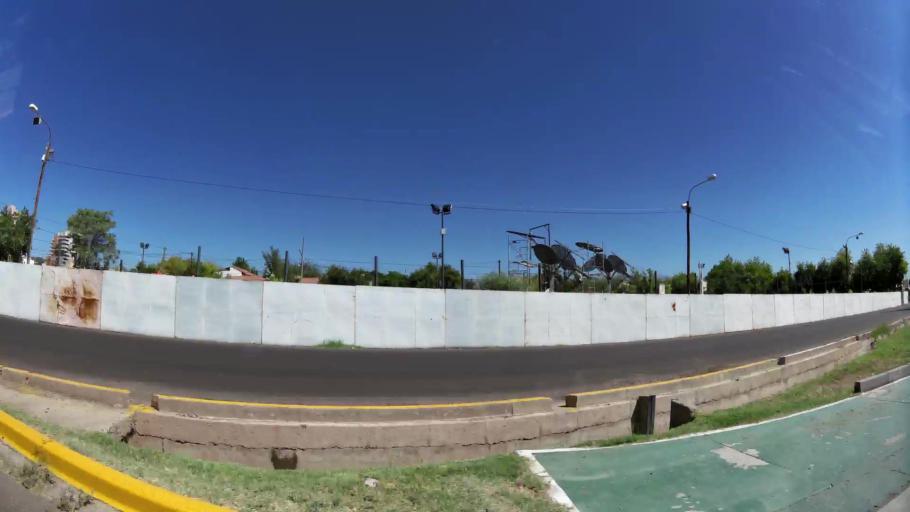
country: AR
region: Mendoza
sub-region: Departamento de Godoy Cruz
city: Godoy Cruz
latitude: -32.9504
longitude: -68.8561
